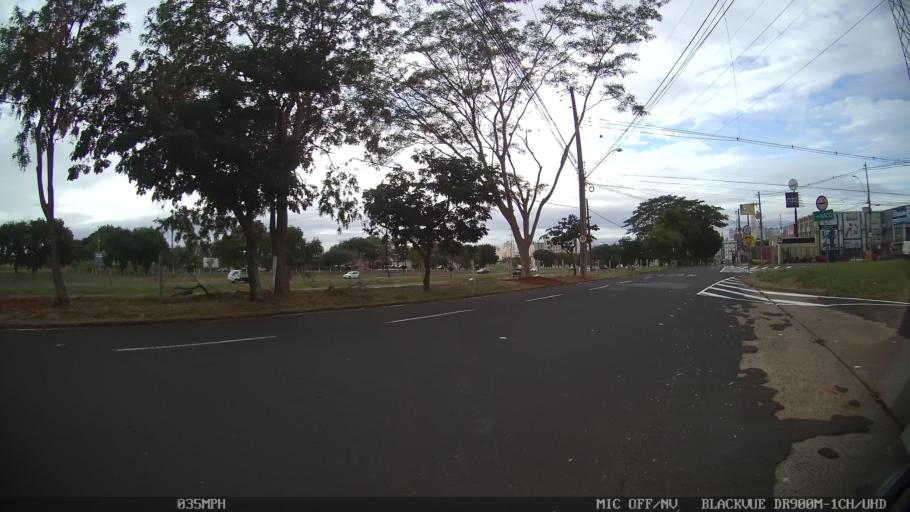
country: BR
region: Sao Paulo
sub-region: Sao Jose Do Rio Preto
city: Sao Jose do Rio Preto
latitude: -20.8253
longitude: -49.4099
